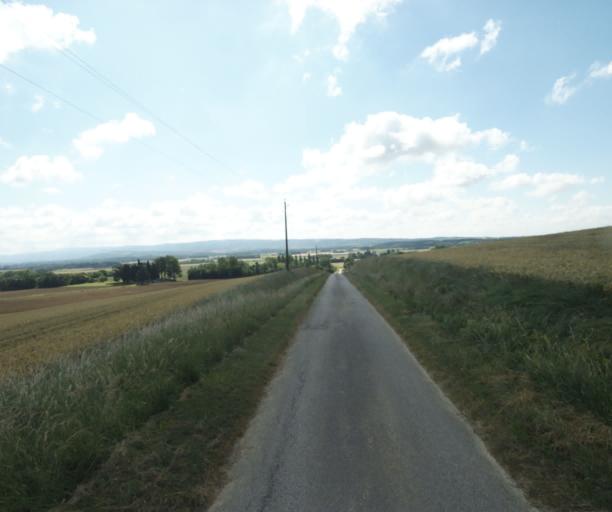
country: FR
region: Midi-Pyrenees
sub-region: Departement de la Haute-Garonne
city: Saint-Felix-Lauragais
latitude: 43.4470
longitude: 1.9041
